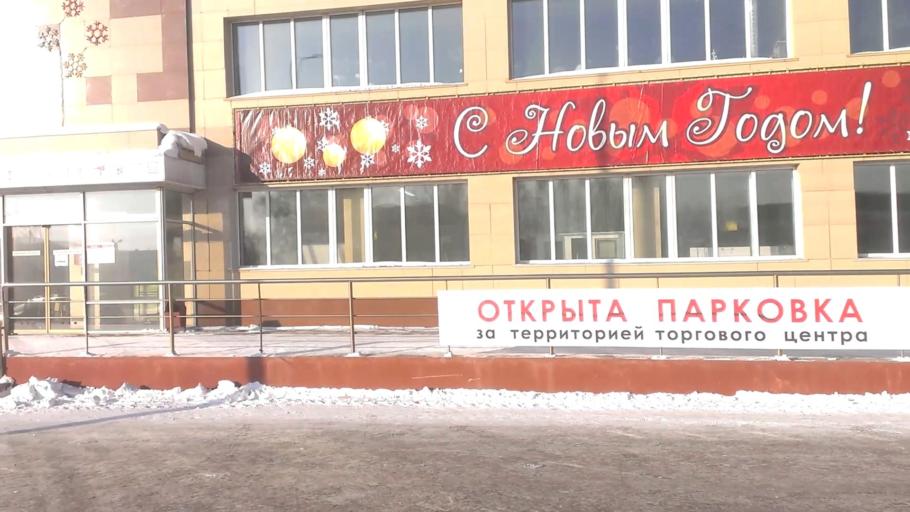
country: RU
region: Altai Krai
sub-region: Gorod Barnaulskiy
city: Barnaul
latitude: 53.3409
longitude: 83.7454
